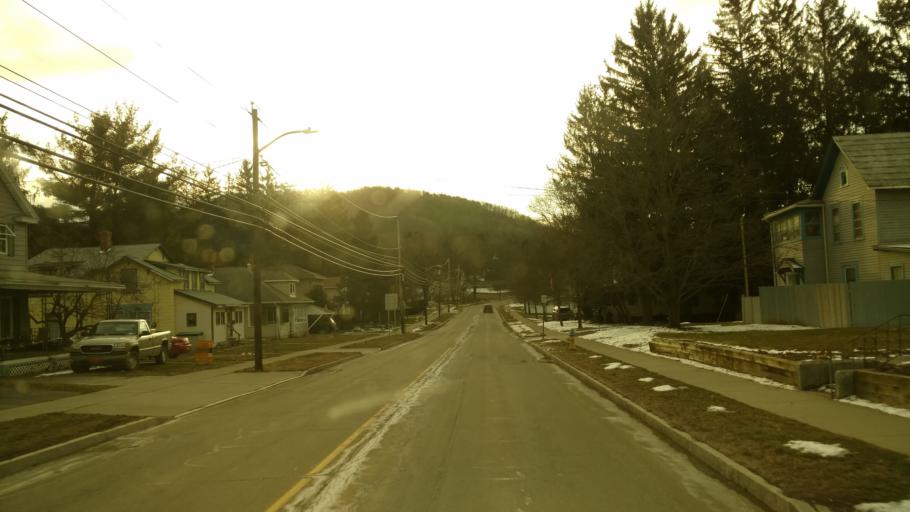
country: US
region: New York
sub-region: Allegany County
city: Wellsville
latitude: 42.1137
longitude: -77.9357
